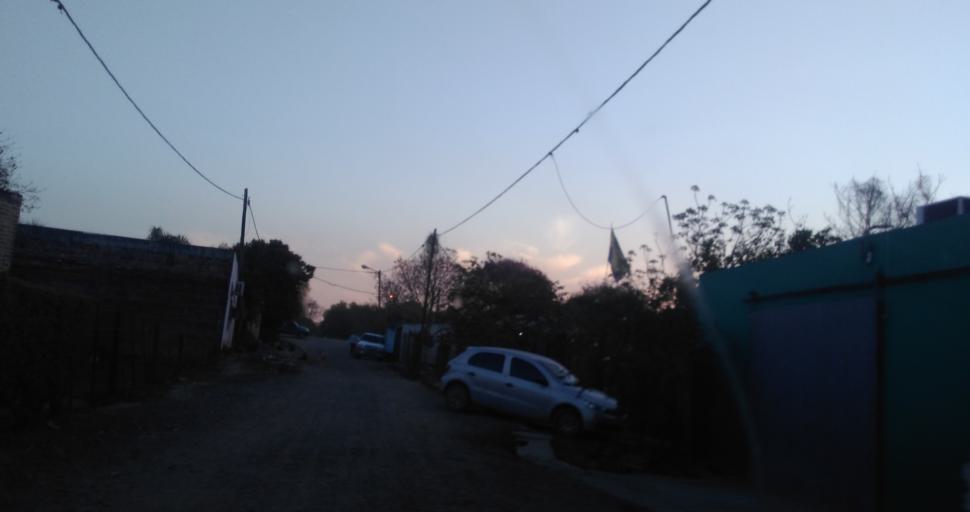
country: AR
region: Chaco
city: Resistencia
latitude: -27.4304
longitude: -58.9882
